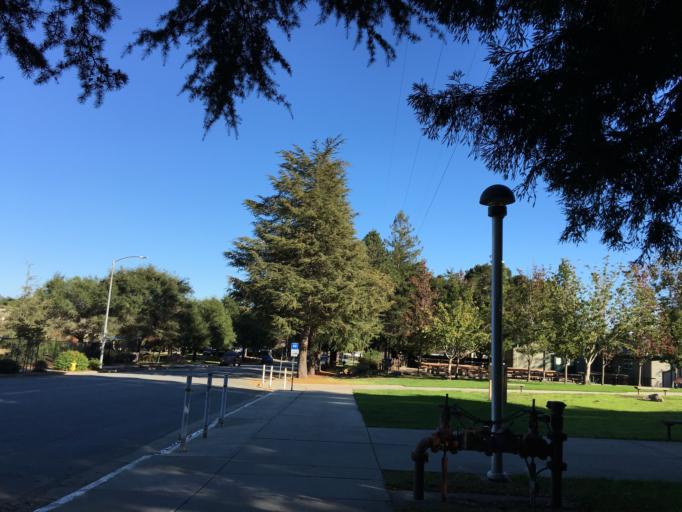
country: US
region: California
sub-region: Santa Cruz County
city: Santa Cruz
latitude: 36.9846
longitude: -122.0387
